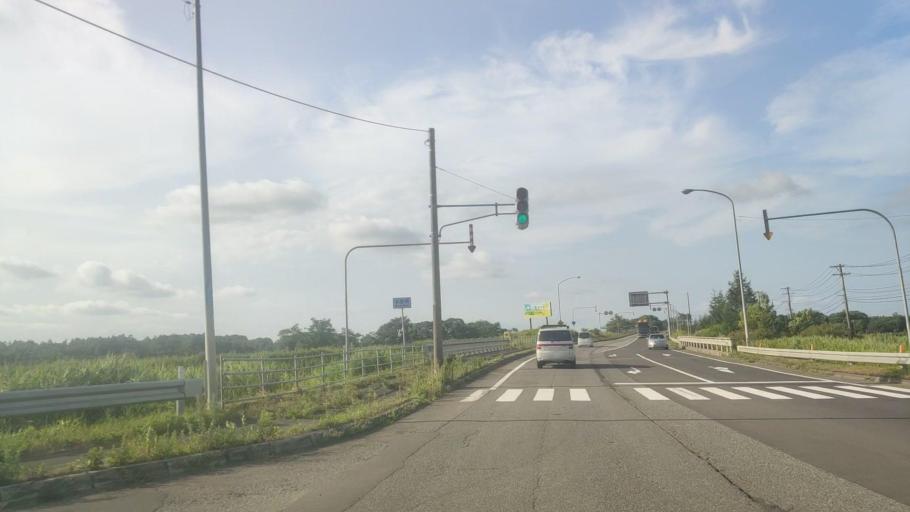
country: JP
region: Hokkaido
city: Chitose
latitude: 42.8855
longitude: 141.8121
